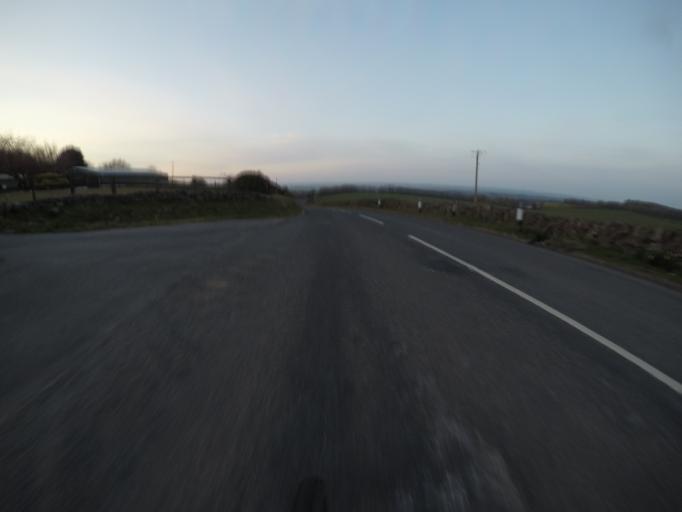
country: GB
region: Scotland
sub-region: South Ayrshire
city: Dundonald
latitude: 55.5651
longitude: -4.6021
